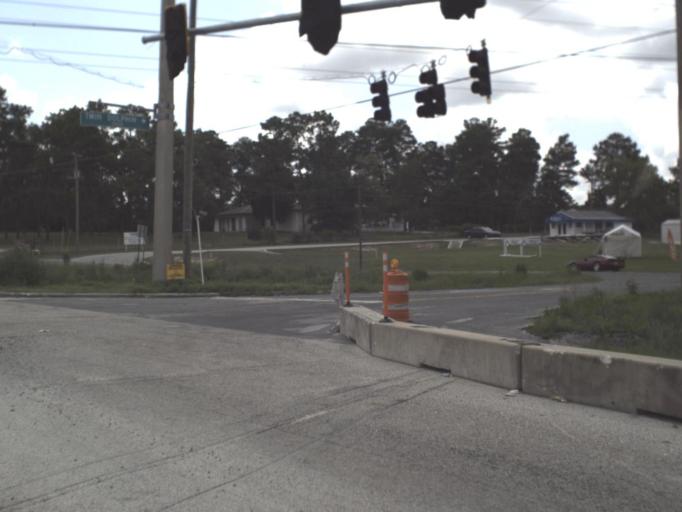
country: US
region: Florida
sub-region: Hernando County
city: Brookridge
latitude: 28.5336
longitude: -82.5001
